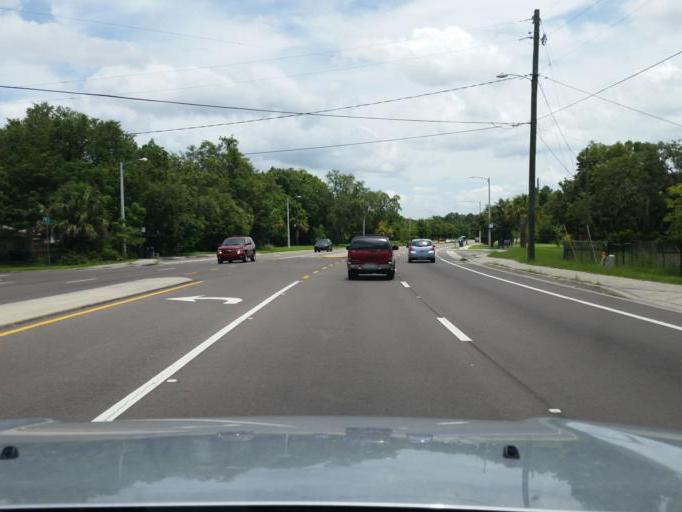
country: US
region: Florida
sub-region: Hillsborough County
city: Temple Terrace
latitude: 28.0111
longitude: -82.4151
